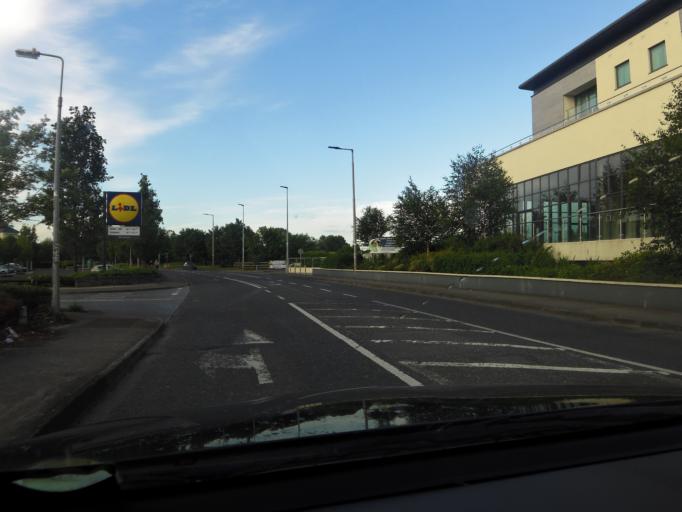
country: IE
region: Connaught
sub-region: County Galway
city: Ballinasloe
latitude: 53.3270
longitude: -8.2200
